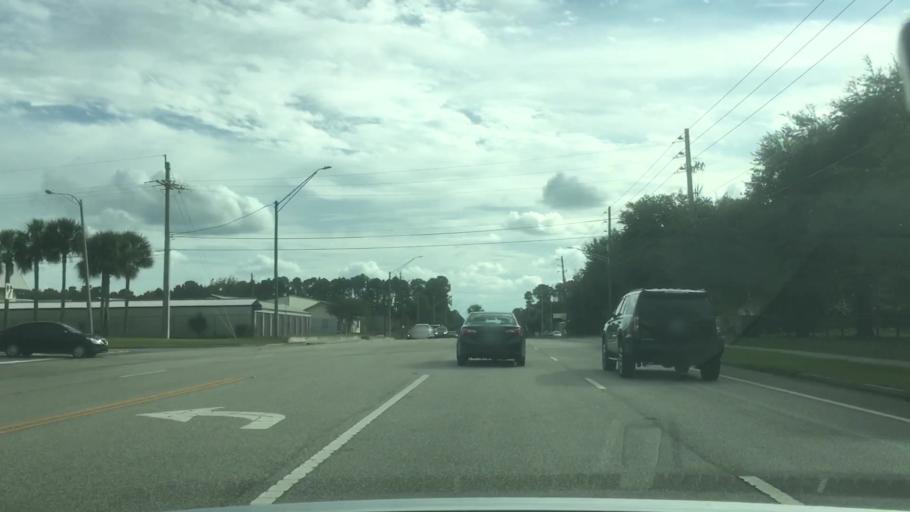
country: US
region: Florida
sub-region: Duval County
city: Atlantic Beach
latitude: 30.3366
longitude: -81.5234
